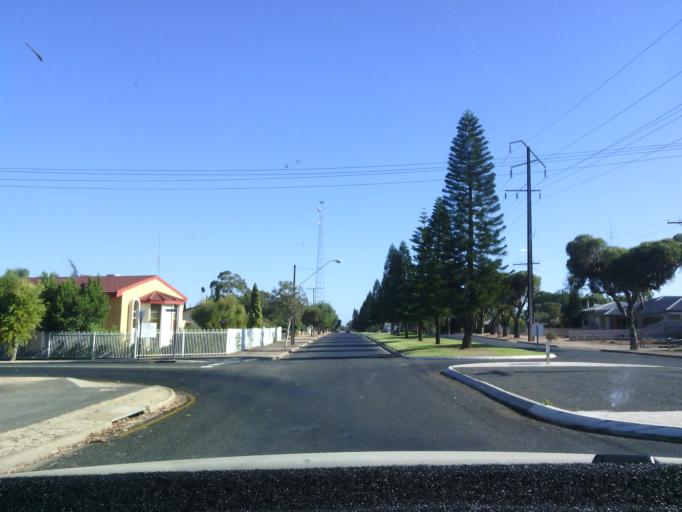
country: AU
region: South Australia
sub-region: Berri and Barmera
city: Berri
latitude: -34.2759
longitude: 140.5971
